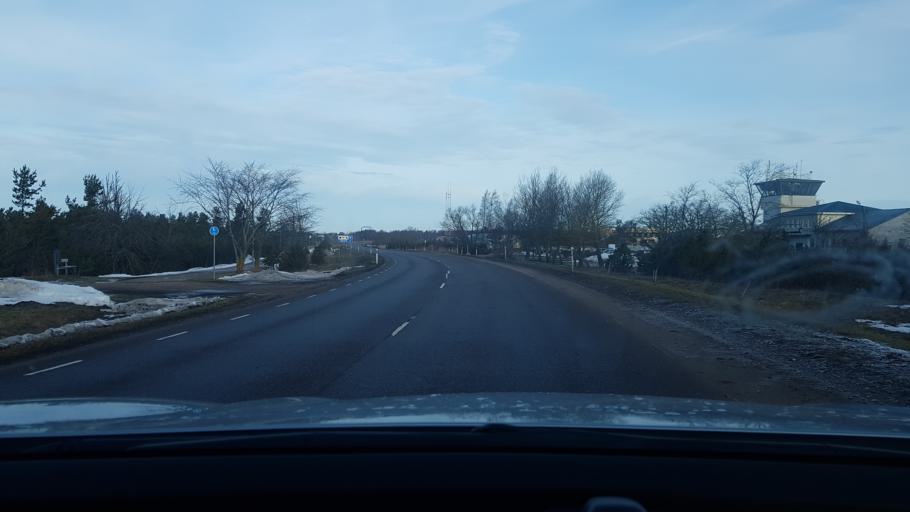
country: EE
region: Saare
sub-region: Kuressaare linn
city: Kuressaare
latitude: 58.2309
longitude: 22.5047
